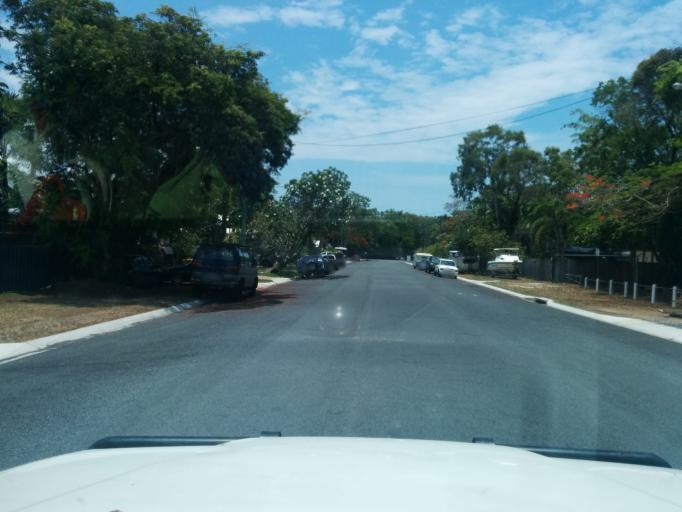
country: AU
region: Queensland
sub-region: Cairns
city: Yorkeys Knob
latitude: -16.8311
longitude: 145.7354
